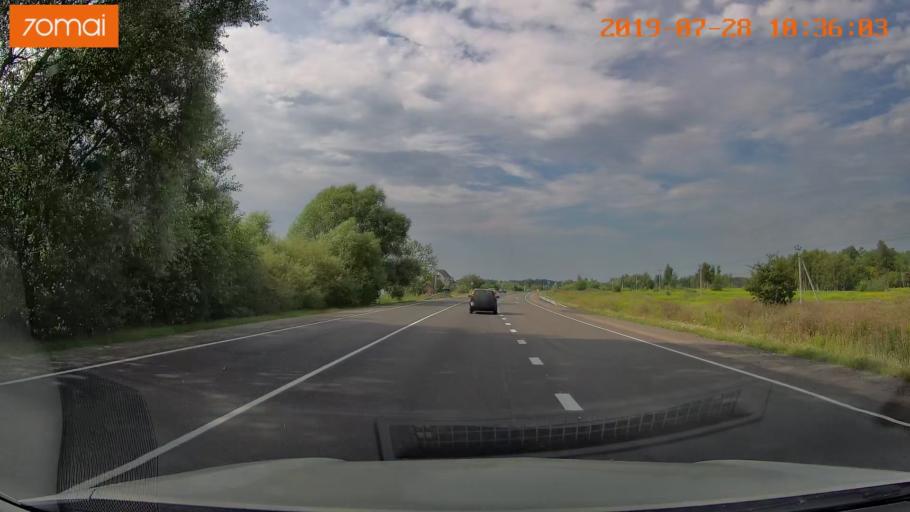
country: RU
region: Kaliningrad
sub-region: Gorod Kaliningrad
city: Kaliningrad
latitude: 54.7409
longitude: 20.4254
